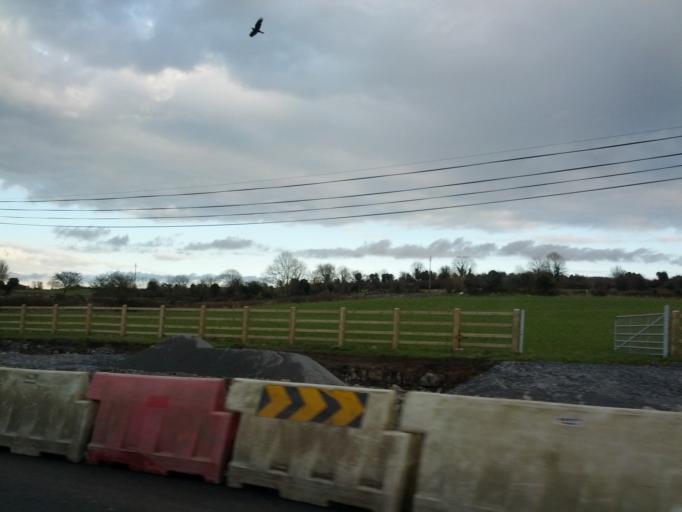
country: IE
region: Connaught
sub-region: County Galway
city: Tuam
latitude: 53.4314
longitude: -8.7571
